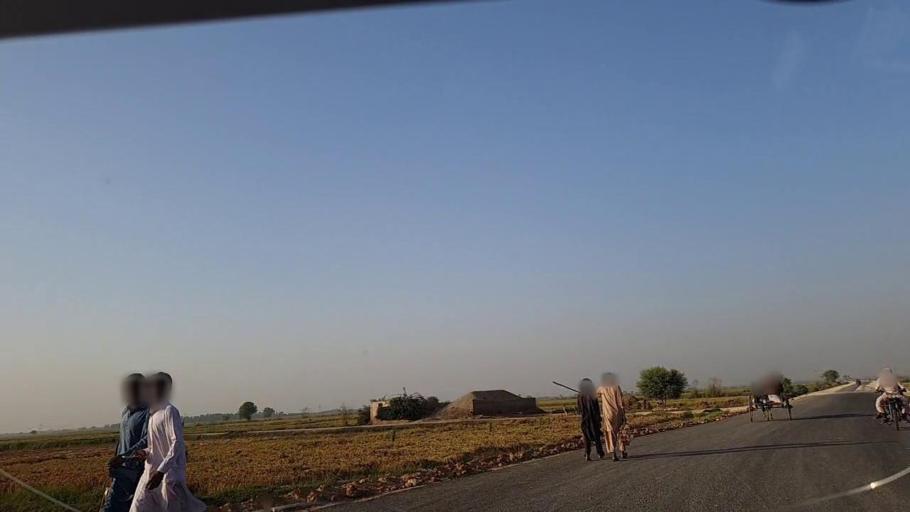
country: PK
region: Sindh
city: Rustam jo Goth
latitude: 27.9755
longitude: 68.8051
